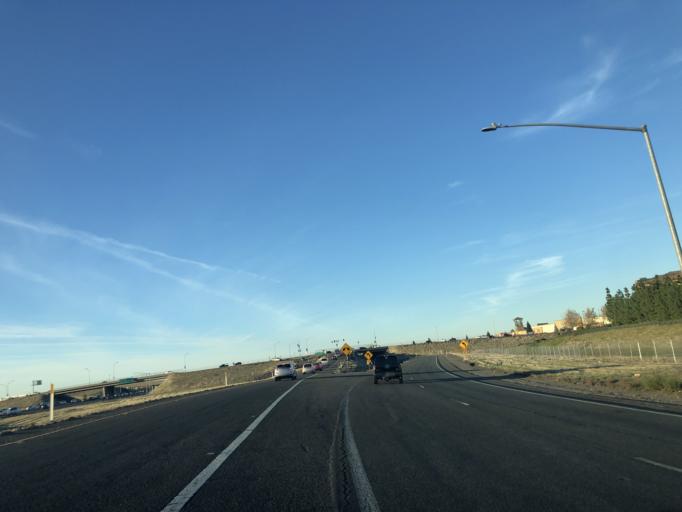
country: US
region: California
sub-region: Placer County
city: Roseville
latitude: 38.7929
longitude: -121.2943
